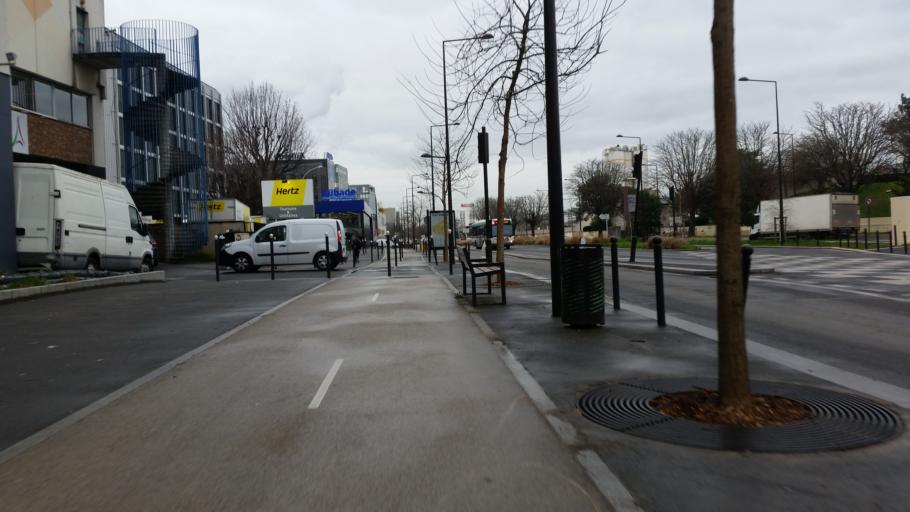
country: FR
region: Ile-de-France
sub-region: Departement du Val-de-Marne
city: Ivry-sur-Seine
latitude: 48.8207
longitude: 2.3947
